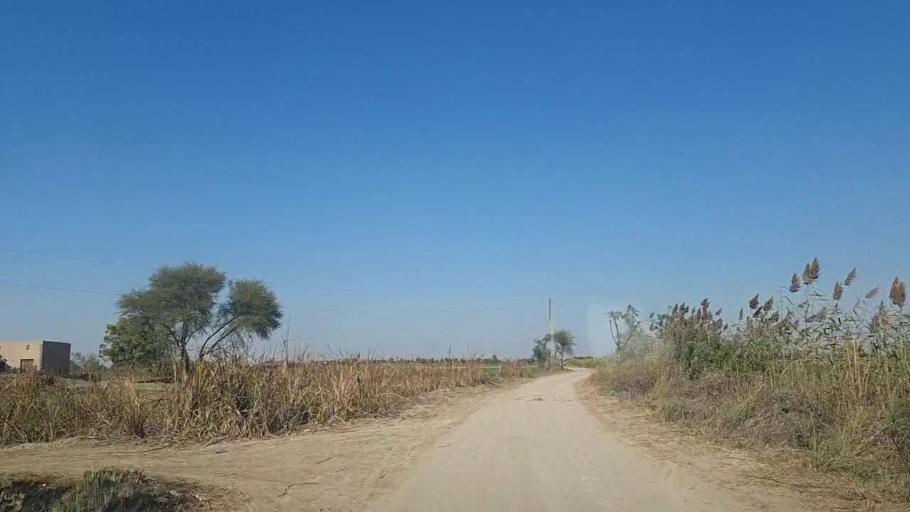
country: PK
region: Sindh
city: Sanghar
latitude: 26.2224
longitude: 68.9646
